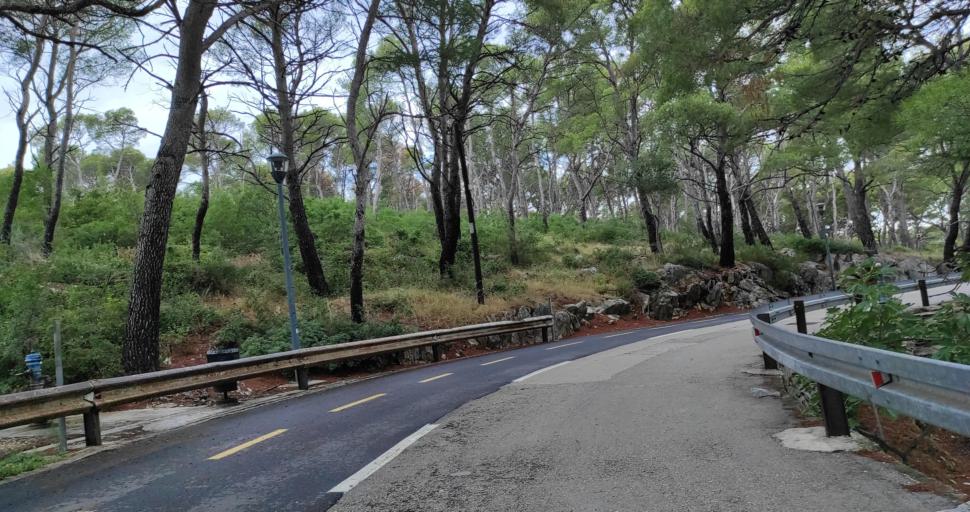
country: HR
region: Splitsko-Dalmatinska
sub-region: Grad Split
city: Split
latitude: 43.5141
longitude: 16.4068
